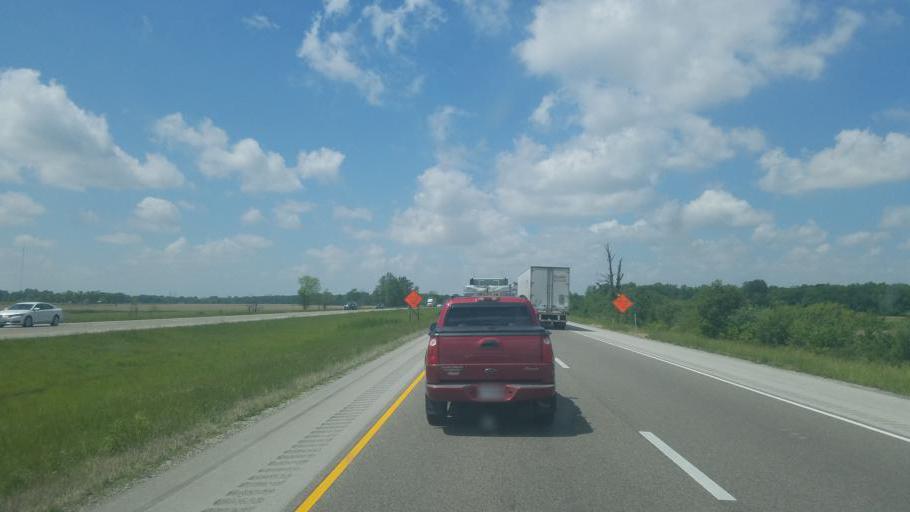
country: US
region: Illinois
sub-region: Cumberland County
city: Toledo
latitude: 39.2283
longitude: -88.2209
